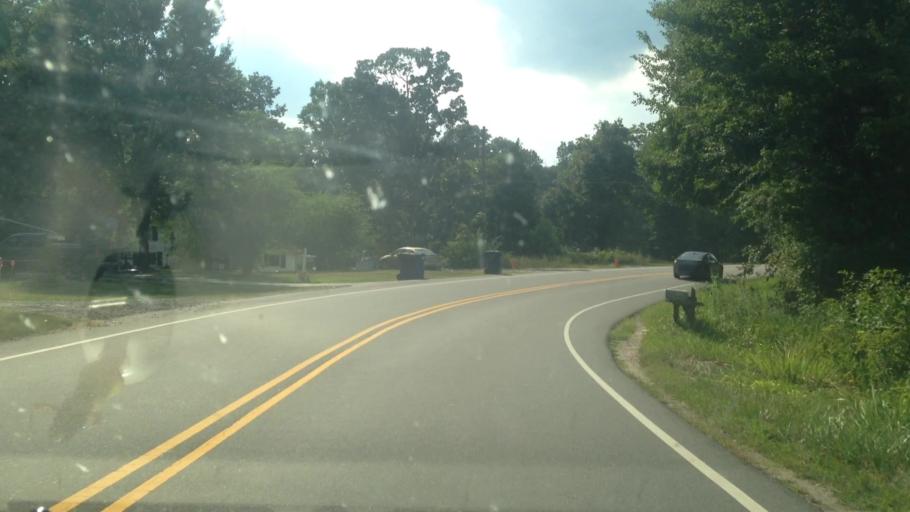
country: US
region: North Carolina
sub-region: Forsyth County
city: Kernersville
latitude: 36.1282
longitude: -80.1148
